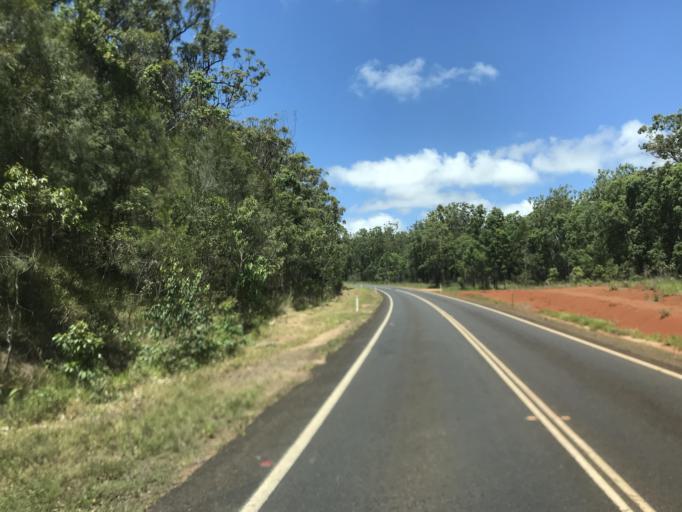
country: AU
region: Queensland
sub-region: Tablelands
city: Ravenshoe
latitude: -17.5377
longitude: 145.4510
